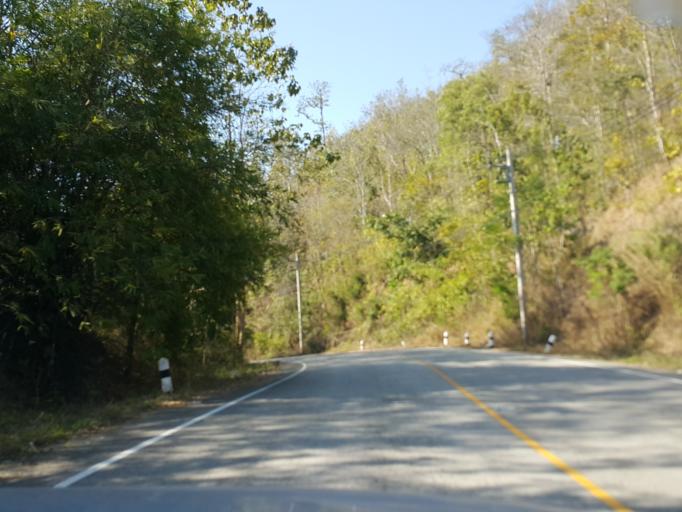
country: TH
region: Chiang Mai
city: Mae Wang
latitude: 18.6197
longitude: 98.7266
